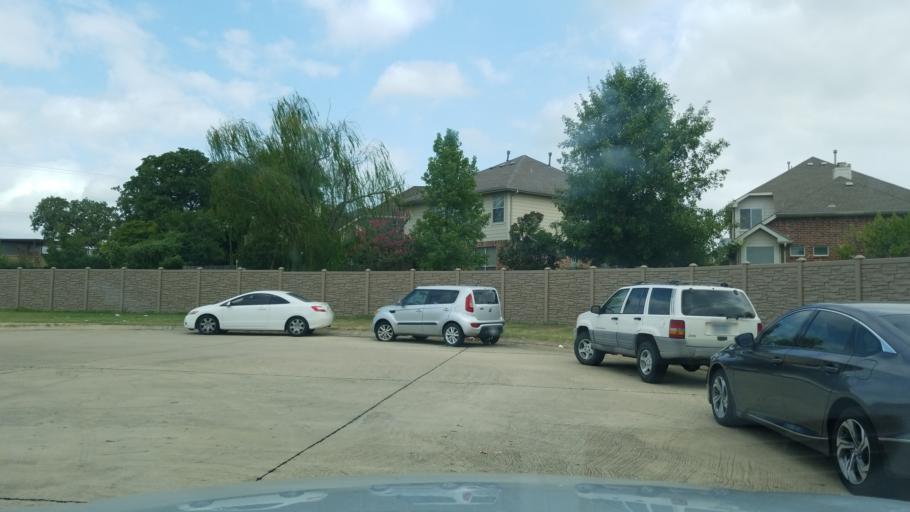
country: US
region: Texas
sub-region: Tarrant County
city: Euless
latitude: 32.8399
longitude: -97.1054
